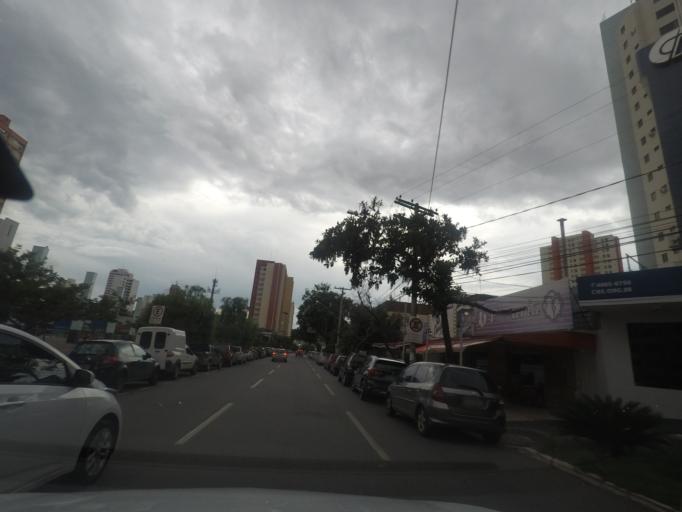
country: BR
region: Goias
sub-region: Goiania
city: Goiania
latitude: -16.6771
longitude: -49.2615
